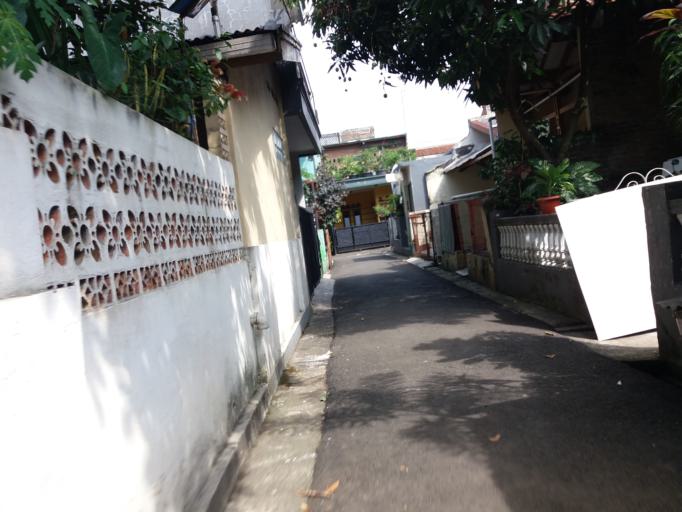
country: ID
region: West Java
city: Bandung
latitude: -6.9181
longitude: 107.6566
